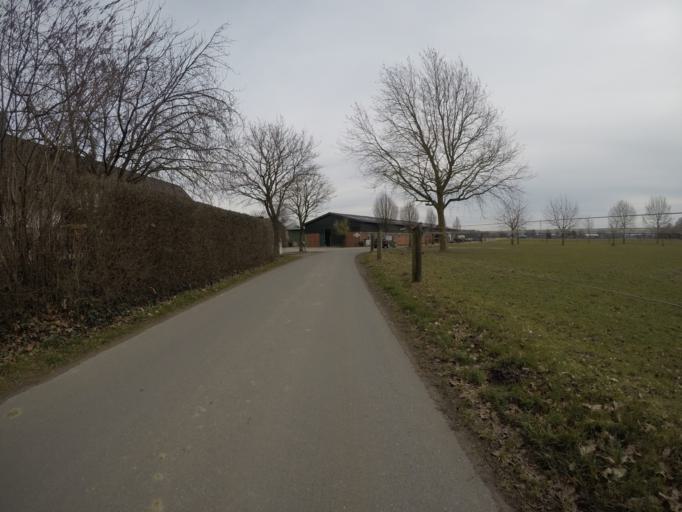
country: DE
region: North Rhine-Westphalia
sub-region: Regierungsbezirk Dusseldorf
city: Hamminkeln
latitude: 51.7820
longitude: 6.5560
